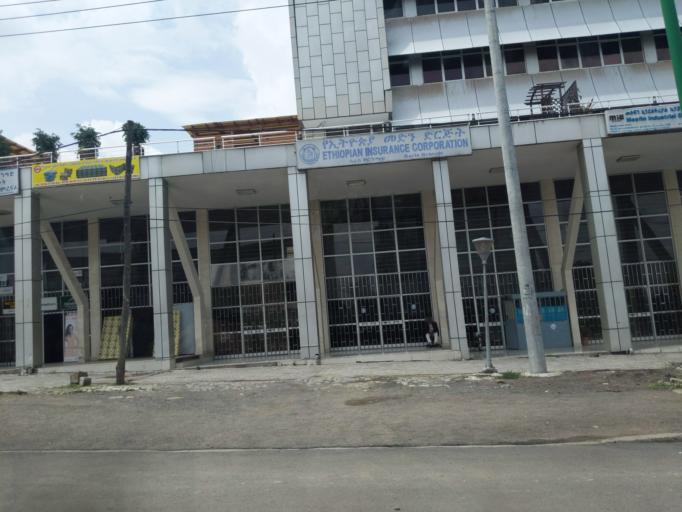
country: ET
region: Adis Abeba
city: Addis Ababa
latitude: 8.9624
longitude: 38.7636
